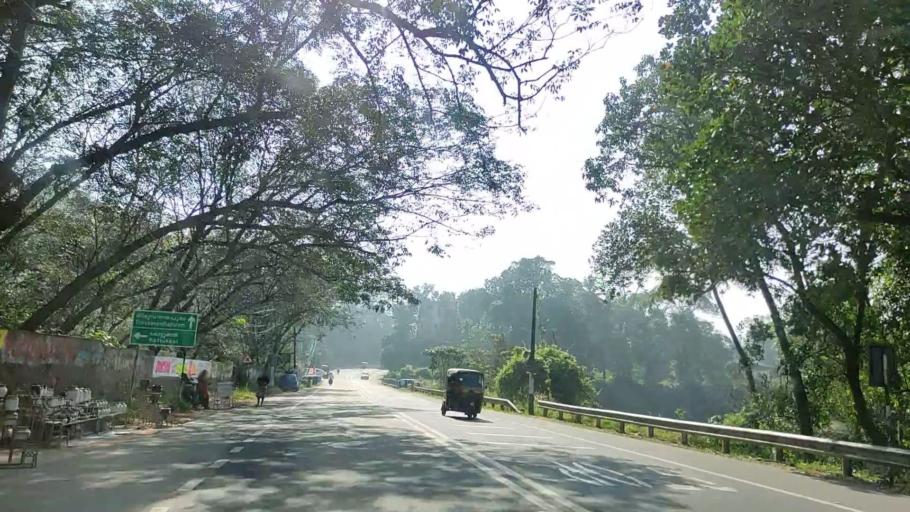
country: IN
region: Kerala
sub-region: Kollam
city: Punalur
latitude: 8.8920
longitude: 76.8653
